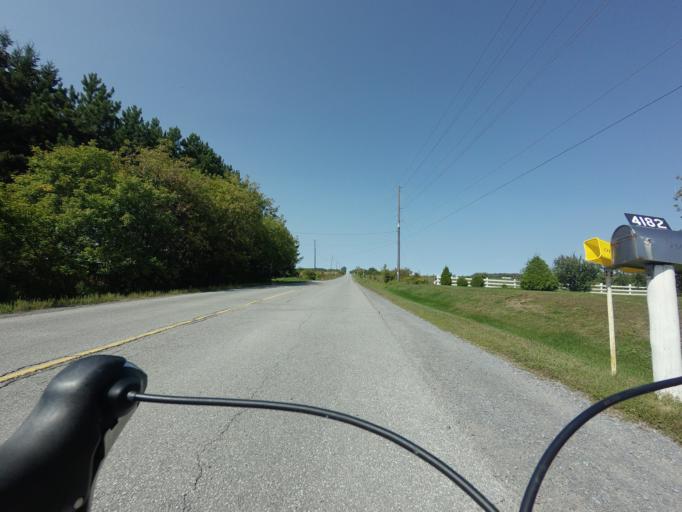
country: CA
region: Ontario
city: Arnprior
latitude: 45.4700
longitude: -76.1091
